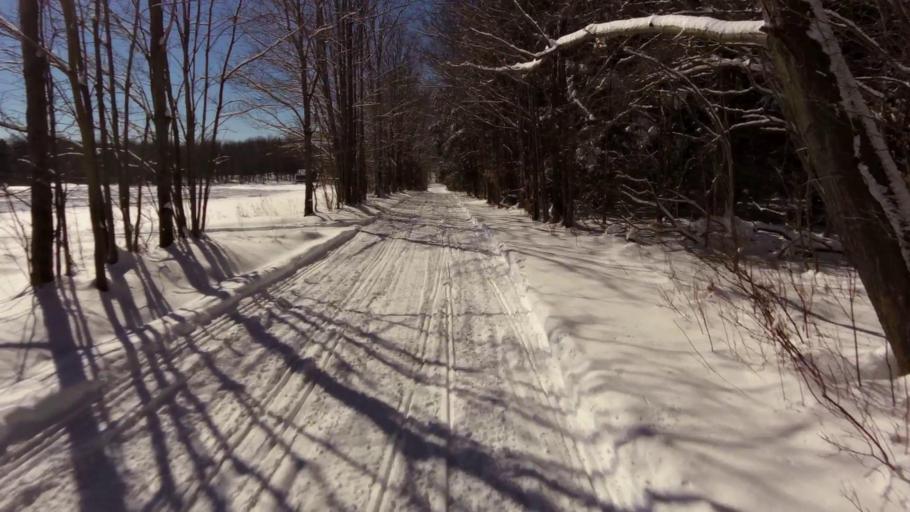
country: US
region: New York
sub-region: Chautauqua County
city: Mayville
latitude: 42.2361
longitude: -79.5195
